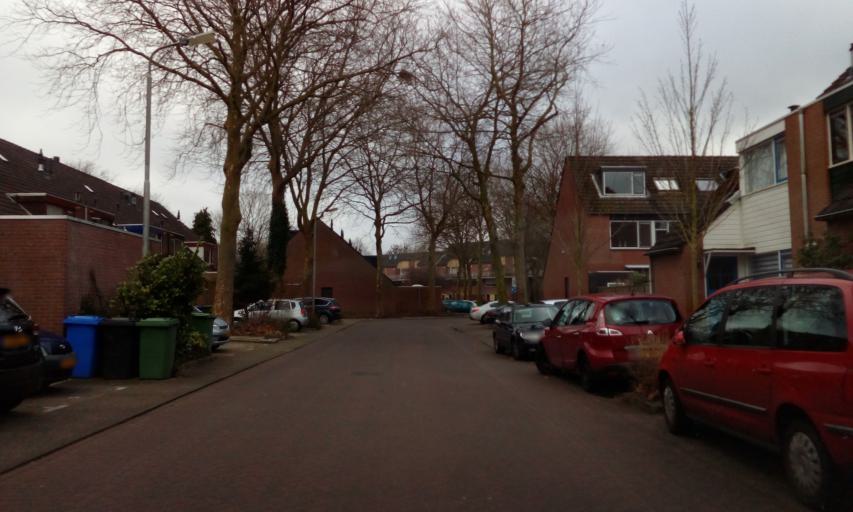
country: NL
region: South Holland
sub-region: Gemeente Delft
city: Delft
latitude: 51.9852
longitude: 4.3567
